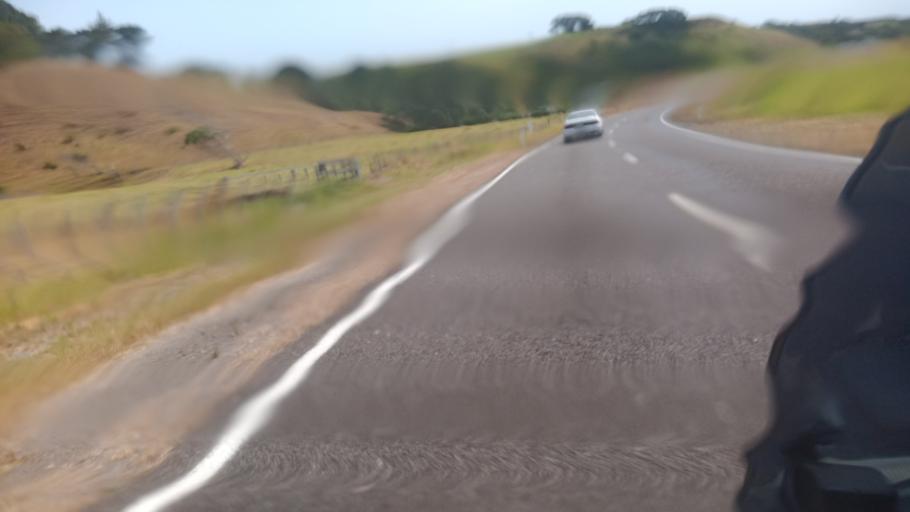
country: NZ
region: Bay of Plenty
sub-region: Opotiki District
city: Opotiki
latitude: -37.6205
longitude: 177.9196
